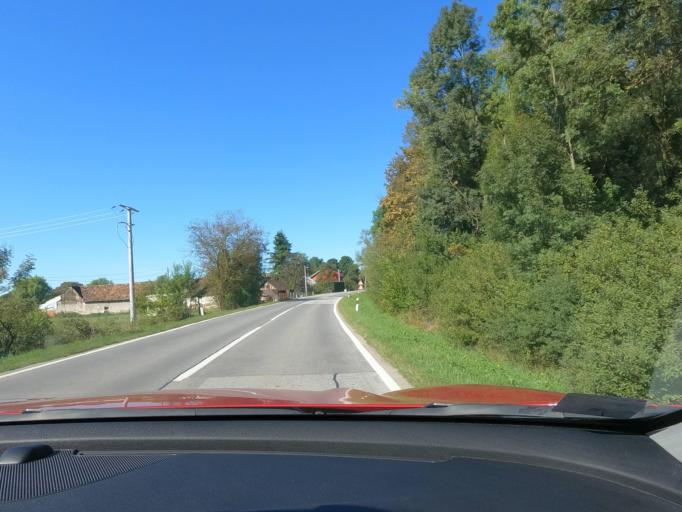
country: HR
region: Sisacko-Moslavacka
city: Budasevo
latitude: 45.4849
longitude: 16.4724
